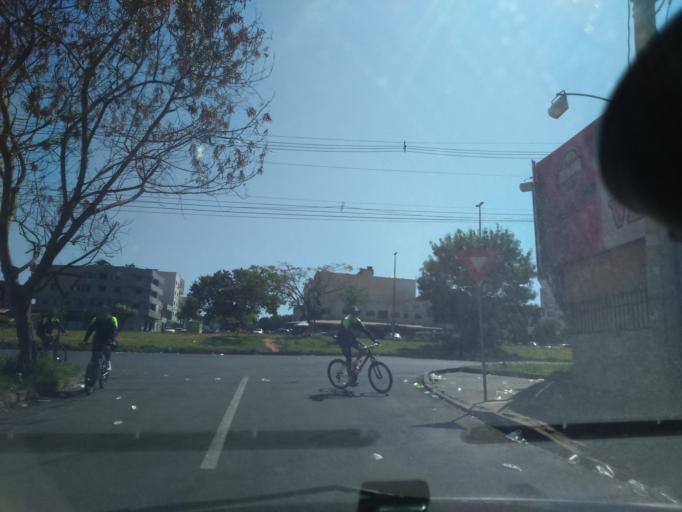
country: BR
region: Federal District
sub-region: Brasilia
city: Brasilia
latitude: -15.8489
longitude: -47.9786
